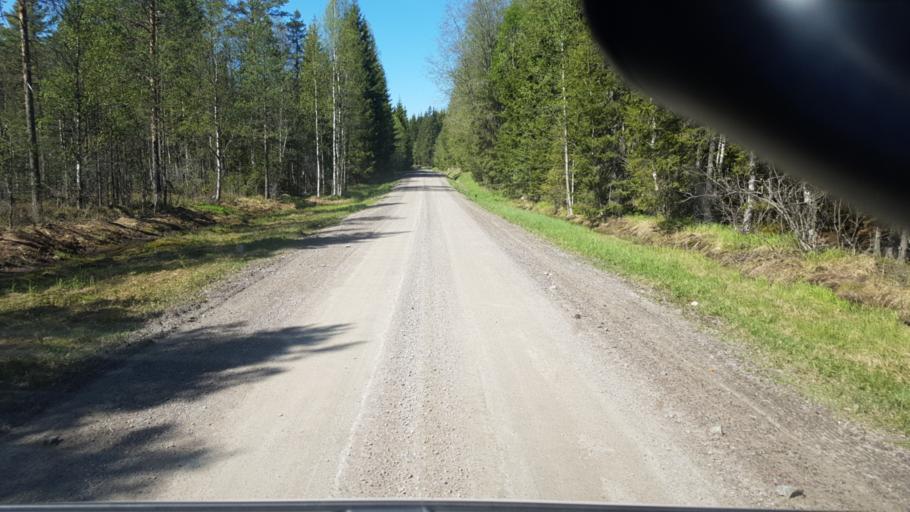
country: SE
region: Vaermland
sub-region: Eda Kommun
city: Charlottenberg
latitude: 59.9830
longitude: 12.4894
